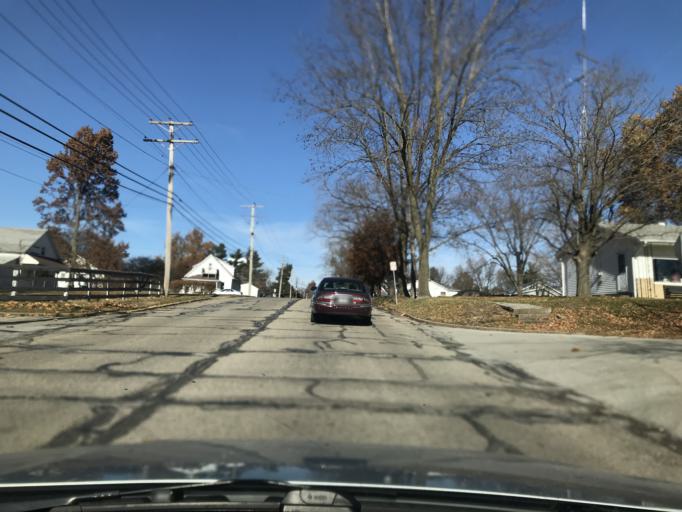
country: US
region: Illinois
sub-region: McDonough County
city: Macomb
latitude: 40.4487
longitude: -90.6674
